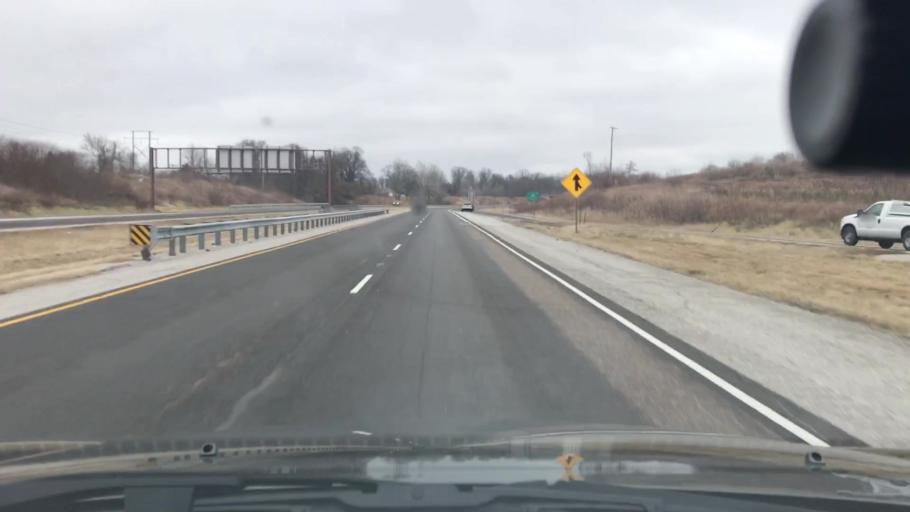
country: US
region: Illinois
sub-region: Madison County
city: Roxana
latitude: 38.8681
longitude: -90.0572
